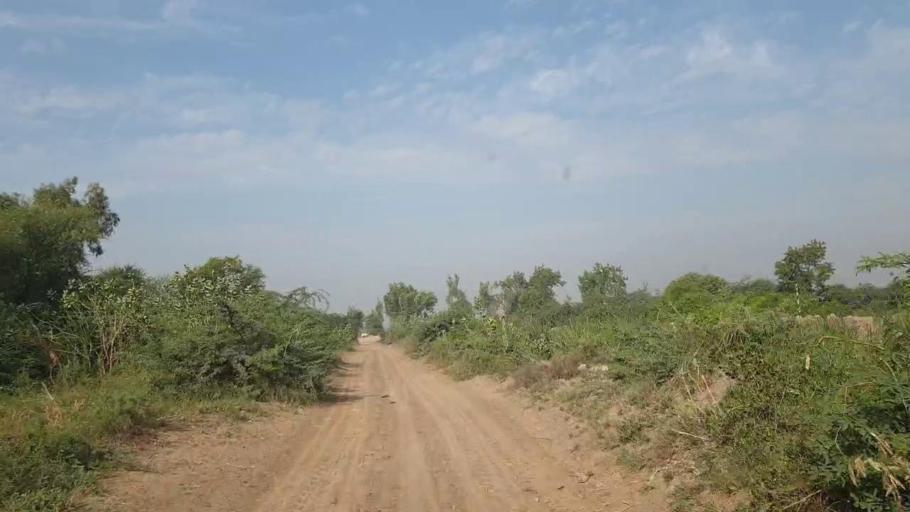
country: PK
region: Sindh
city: Tando Bago
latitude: 24.8707
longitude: 68.9720
